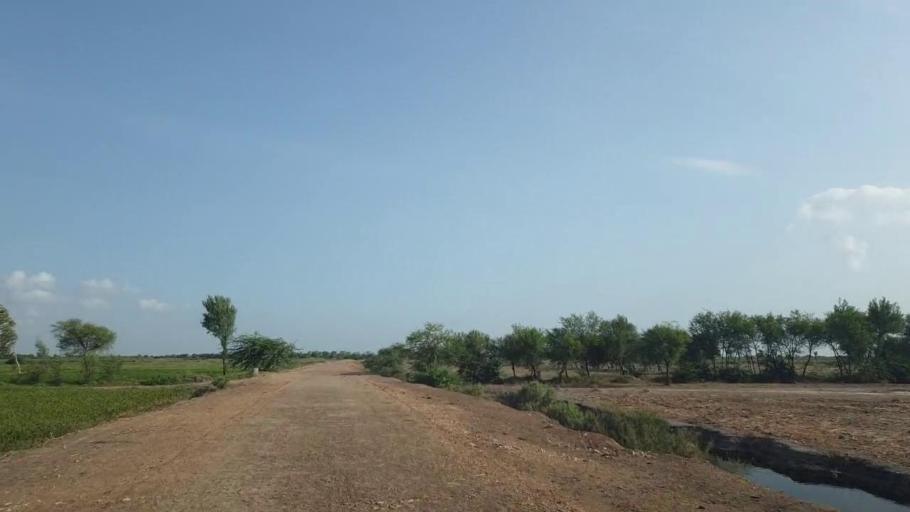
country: PK
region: Sindh
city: Kadhan
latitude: 24.6067
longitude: 69.0879
